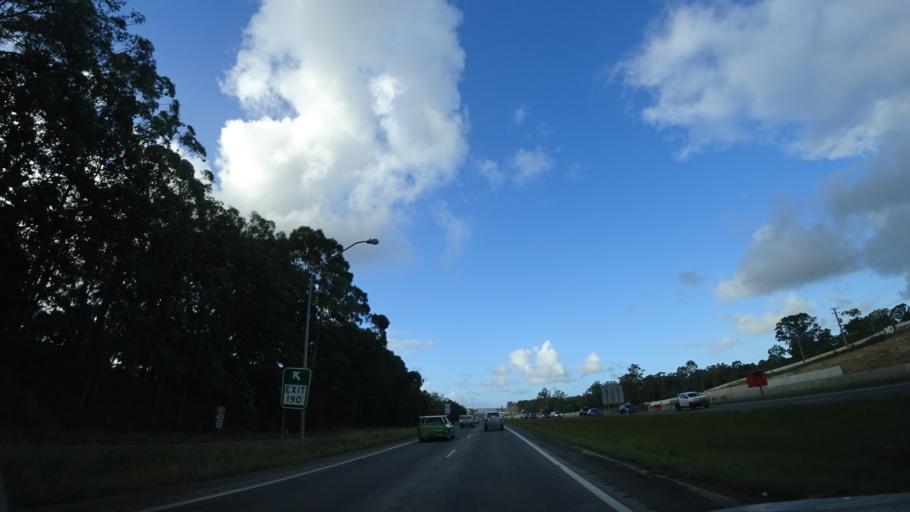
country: AU
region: Queensland
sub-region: Sunshine Coast
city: Little Mountain
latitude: -26.7618
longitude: 153.0461
